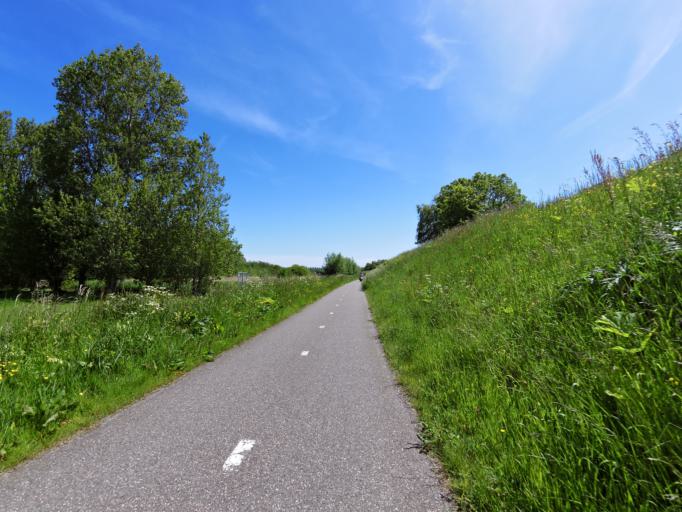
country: NL
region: South Holland
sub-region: Gemeente Hellevoetsluis
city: Nieuw-Helvoet
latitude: 51.8593
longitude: 4.0812
